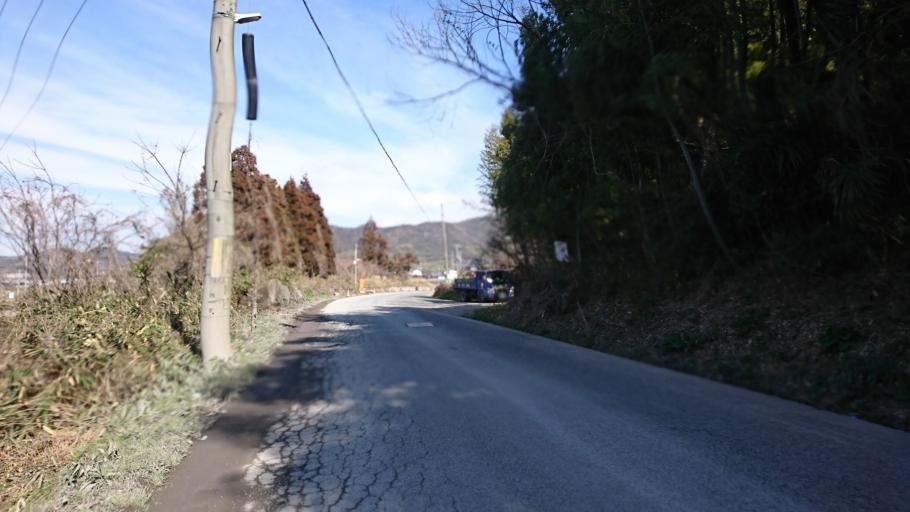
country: JP
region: Hyogo
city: Kakogawacho-honmachi
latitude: 34.8225
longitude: 134.8326
